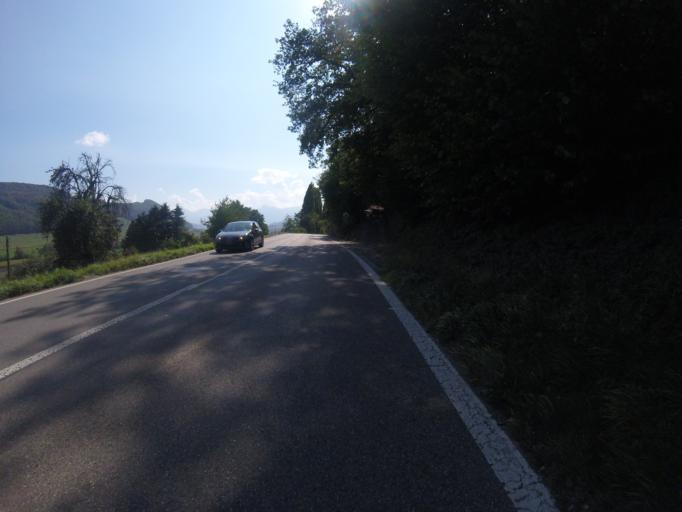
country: CH
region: Bern
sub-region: Bern-Mittelland District
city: Toffen
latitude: 46.8745
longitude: 7.4924
